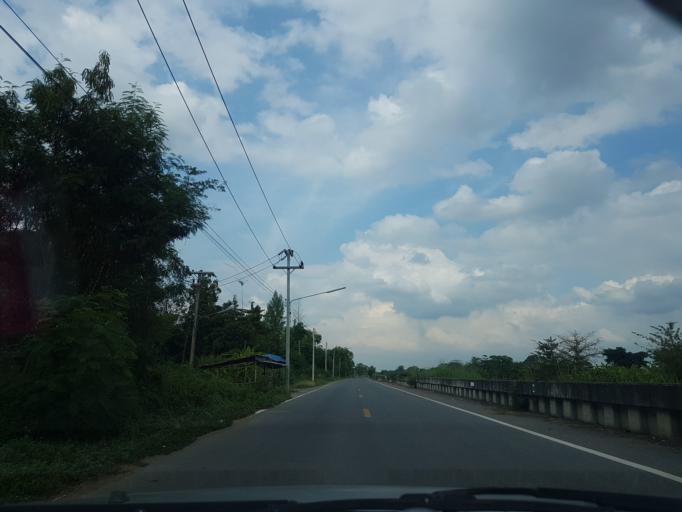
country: TH
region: Pathum Thani
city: Nong Suea
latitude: 14.1868
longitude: 100.8915
